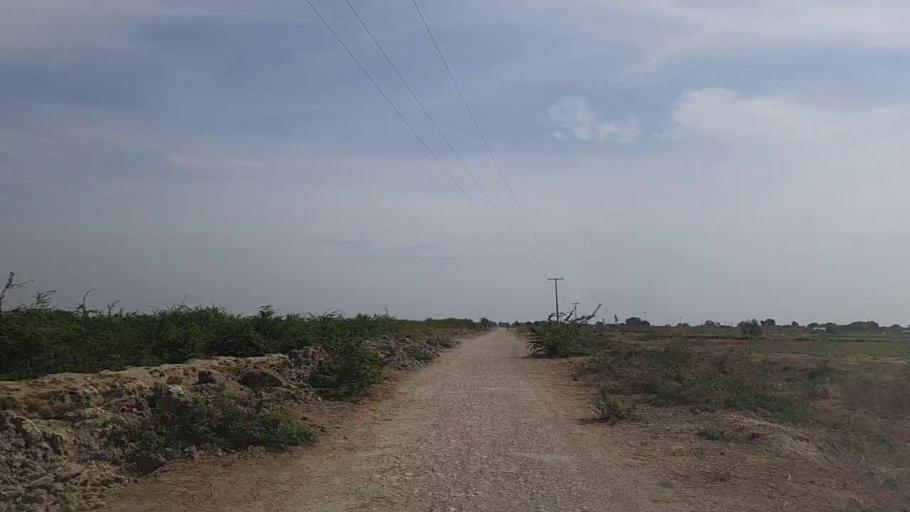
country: PK
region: Sindh
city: Samaro
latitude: 25.2055
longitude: 69.4605
